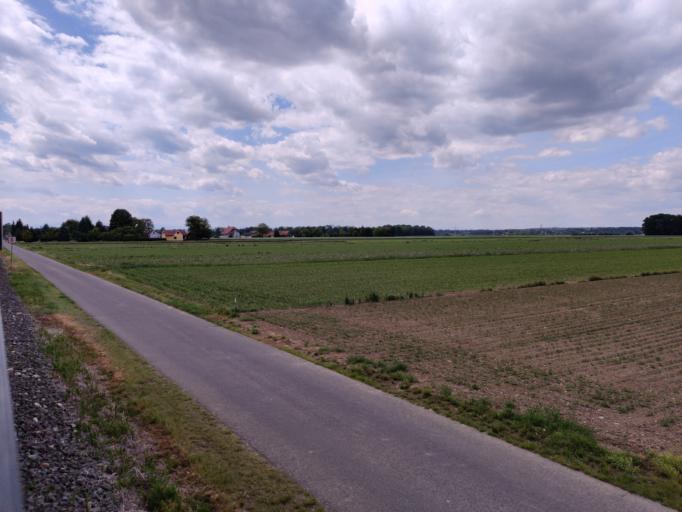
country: AT
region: Styria
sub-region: Politischer Bezirk Suedoststeiermark
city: Weinburg am Sassbach
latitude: 46.7146
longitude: 15.7281
